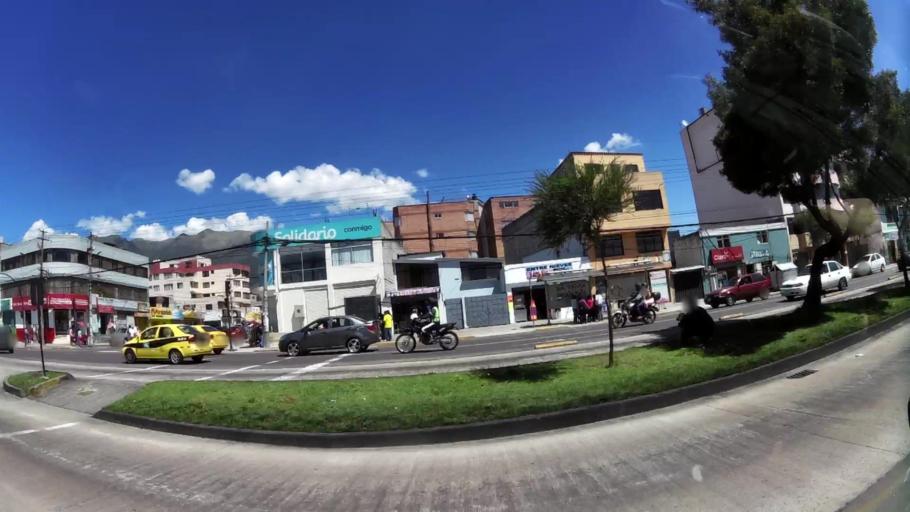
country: EC
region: Pichincha
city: Quito
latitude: -0.1290
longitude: -78.4940
